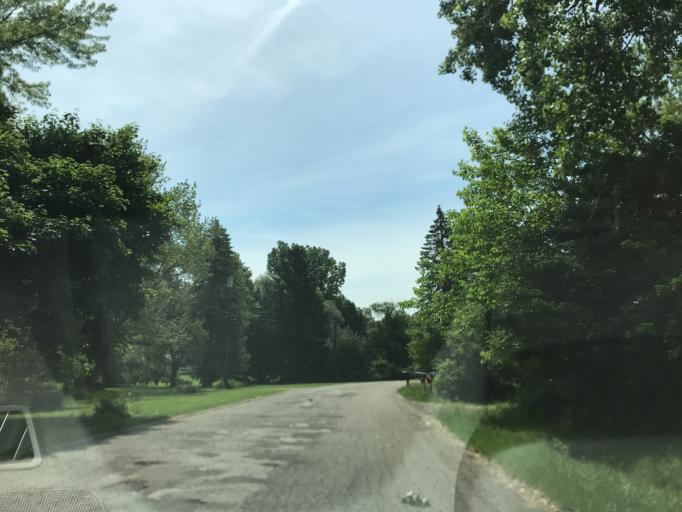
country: US
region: Michigan
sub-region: Oakland County
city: Bingham Farms
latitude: 42.4769
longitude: -83.2713
